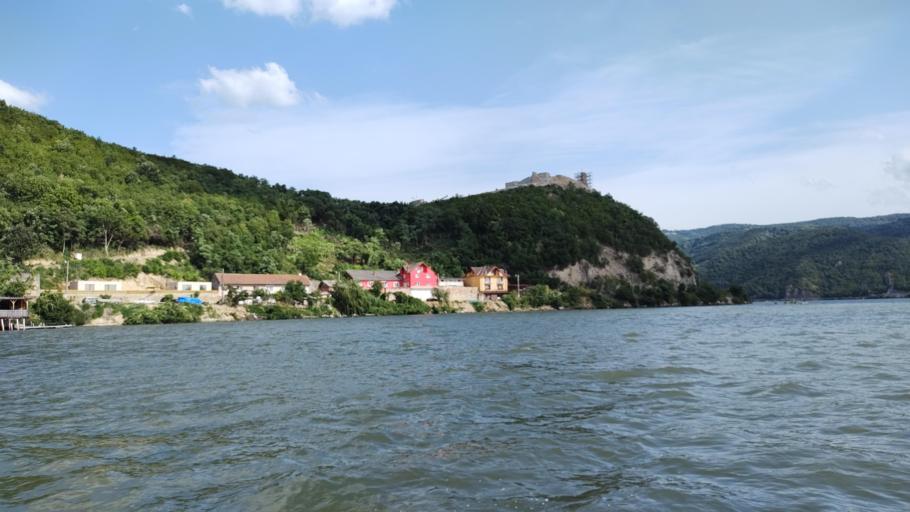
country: RO
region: Caras-Severin
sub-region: Comuna Pescari
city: Coronini
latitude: 44.6760
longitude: 21.6781
